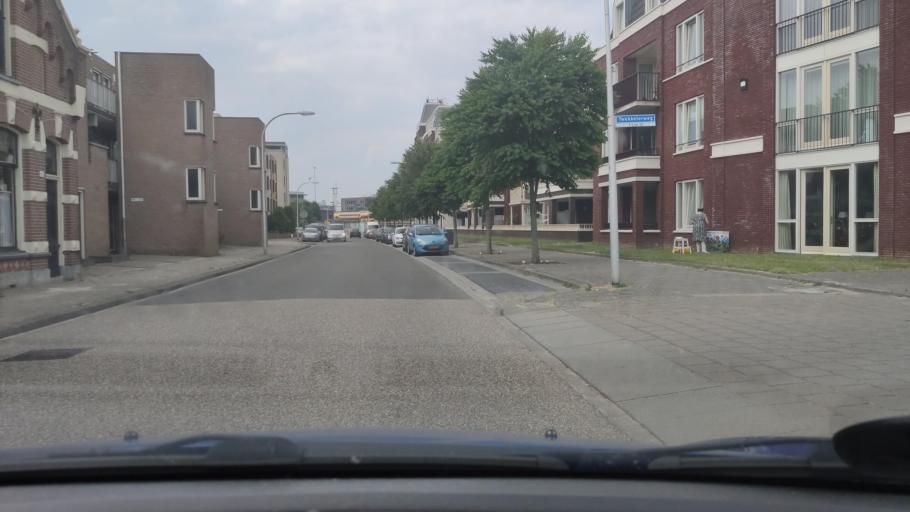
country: NL
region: Overijssel
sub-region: Gemeente Hengelo
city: Hengelo
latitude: 52.2593
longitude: 6.8000
